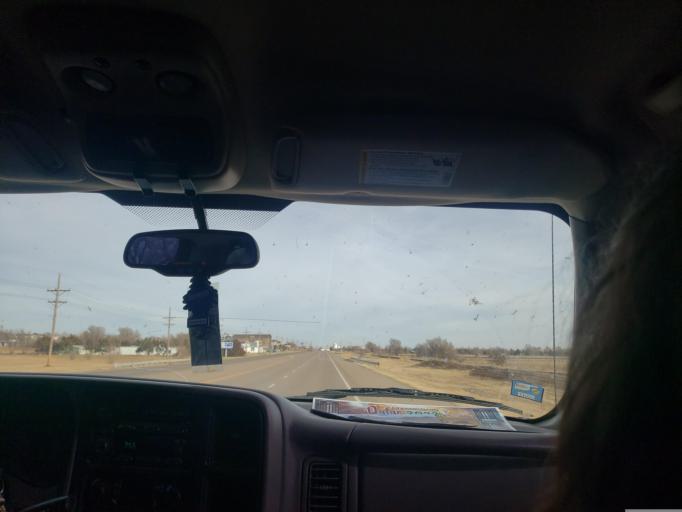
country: US
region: Kansas
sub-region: Ford County
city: Dodge City
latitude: 37.7552
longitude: -100.0628
